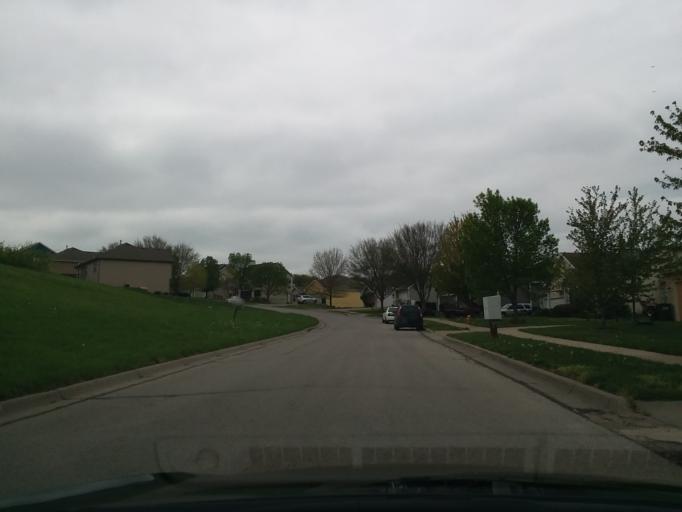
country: US
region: Kansas
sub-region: Douglas County
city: Lawrence
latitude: 38.9904
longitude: -95.2819
